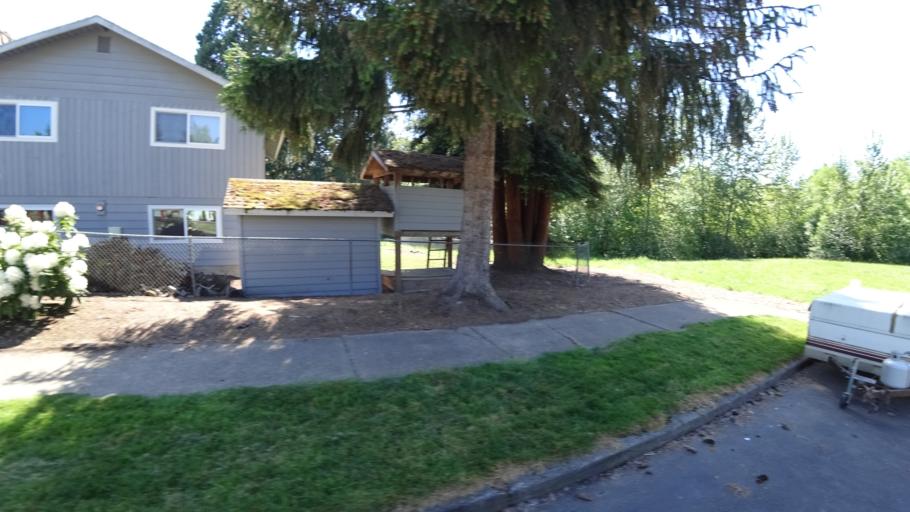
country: US
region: Oregon
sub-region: Washington County
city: Rockcreek
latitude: 45.5549
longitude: -122.8740
